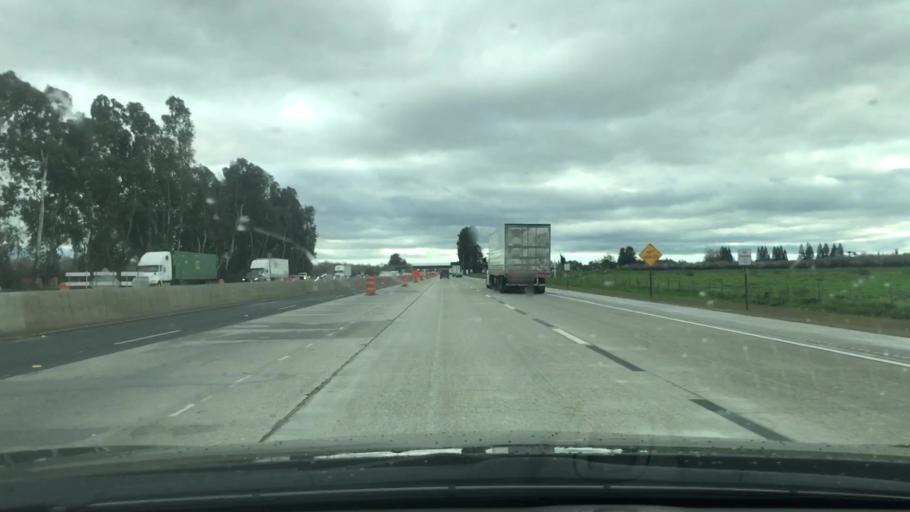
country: US
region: California
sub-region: Stanislaus County
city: Turlock
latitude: 37.4623
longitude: -120.8199
